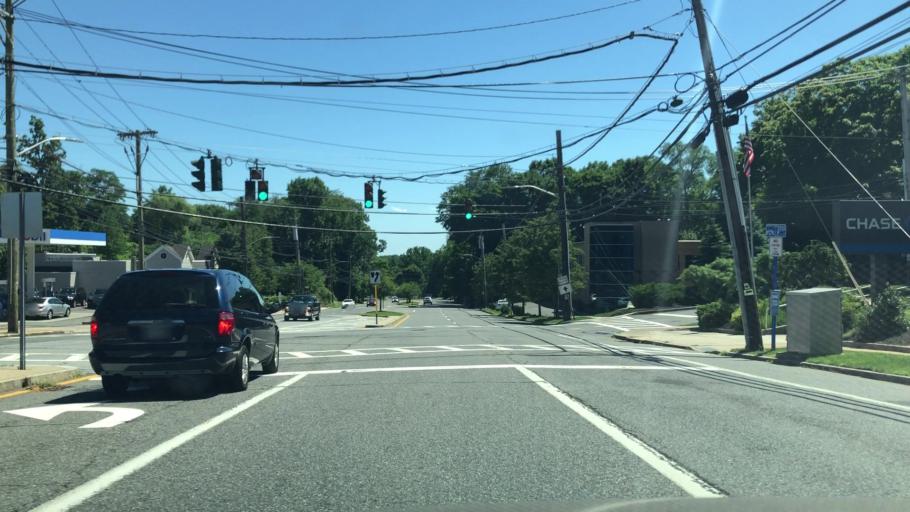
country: US
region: New York
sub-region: Westchester County
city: Scarsdale
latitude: 40.9924
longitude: -73.7462
